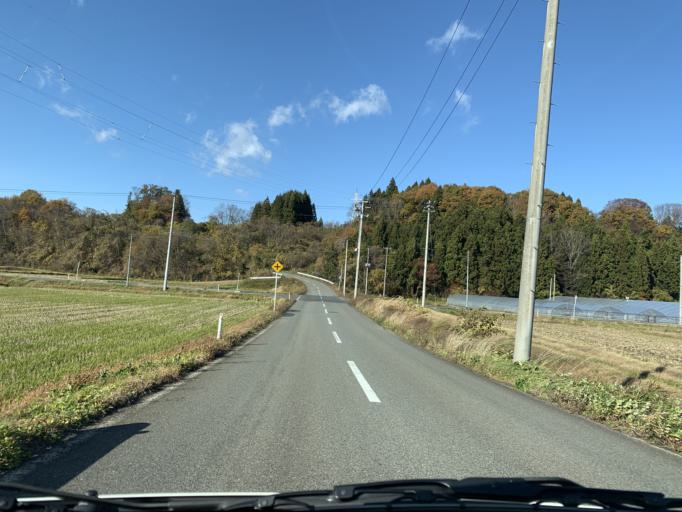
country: JP
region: Iwate
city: Mizusawa
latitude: 39.0914
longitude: 141.1253
